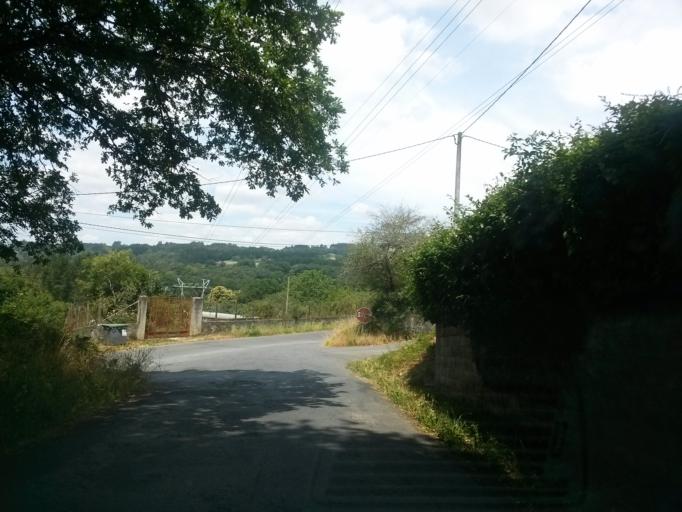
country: ES
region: Galicia
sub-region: Provincia de Lugo
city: Lugo
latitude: 43.0283
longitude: -7.5847
